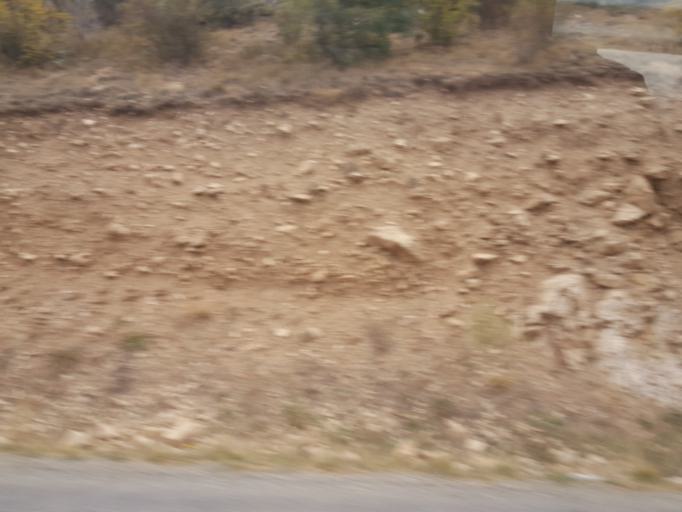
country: TR
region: Yozgat
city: Cekerek
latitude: 40.1992
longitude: 35.4553
